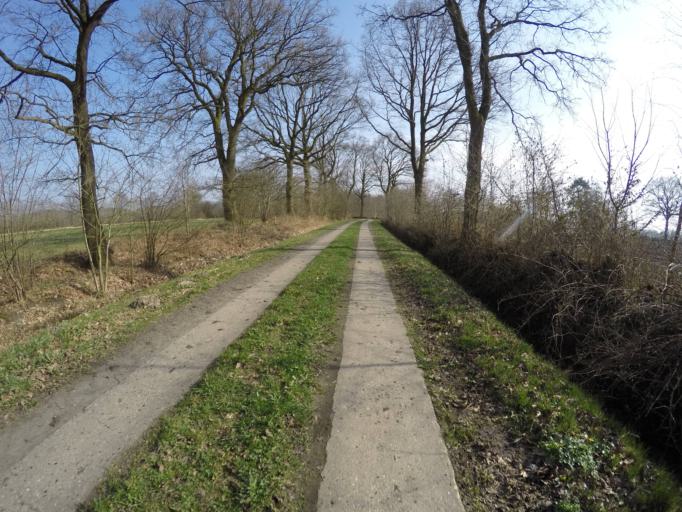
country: DE
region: Schleswig-Holstein
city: Borstel-Hohenraden
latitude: 53.7206
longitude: 9.8345
